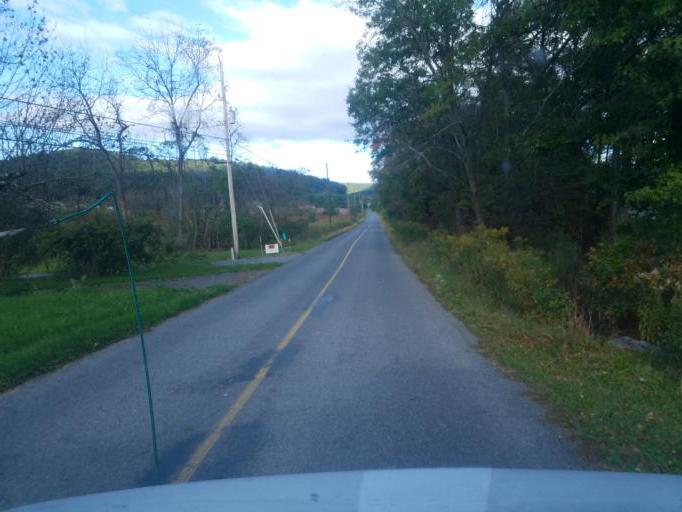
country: US
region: Pennsylvania
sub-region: Adams County
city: Biglerville
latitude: 39.8901
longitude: -77.3491
